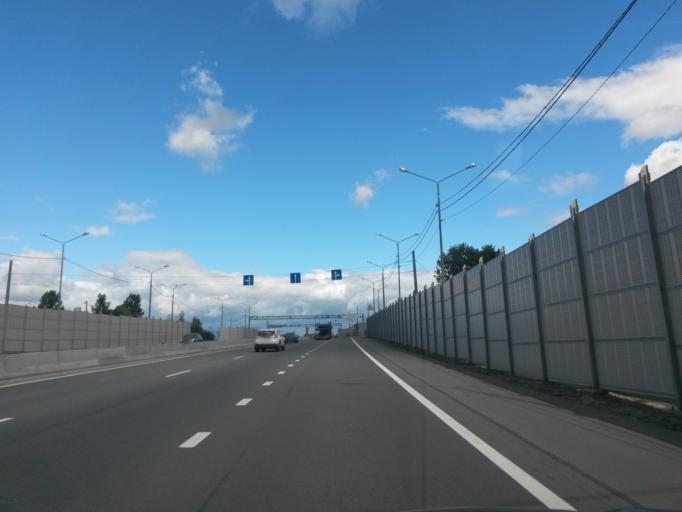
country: RU
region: Jaroslavl
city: Yaroslavl
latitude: 57.7054
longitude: 39.9010
